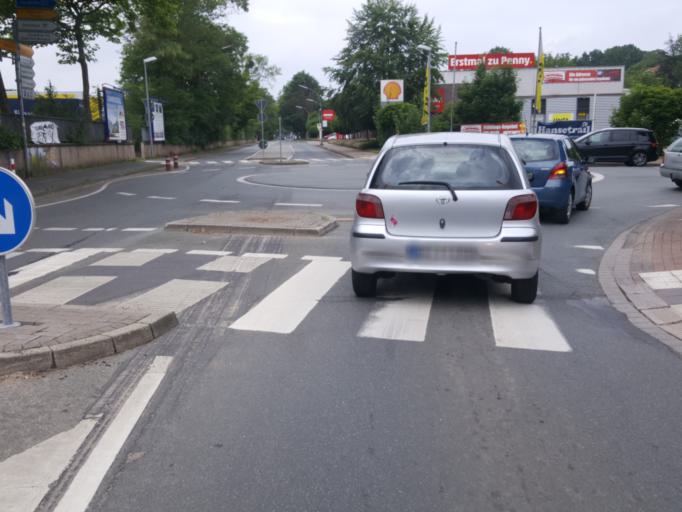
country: DE
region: North Rhine-Westphalia
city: Bad Oeynhausen
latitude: 52.1978
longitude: 8.8081
